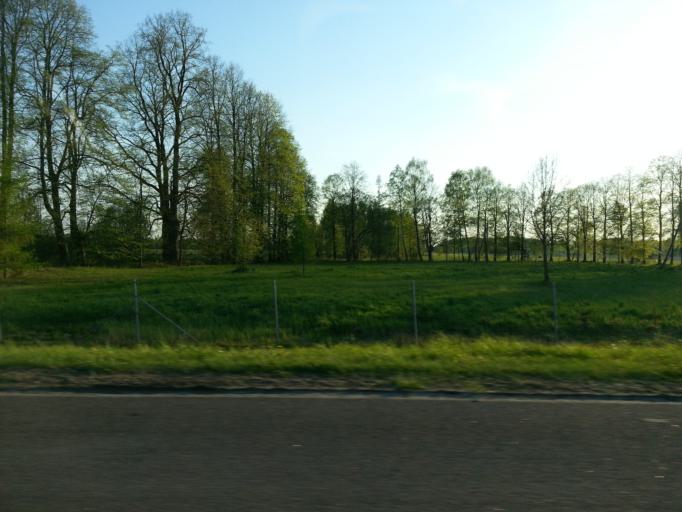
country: LT
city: Sirvintos
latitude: 54.9800
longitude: 24.9395
